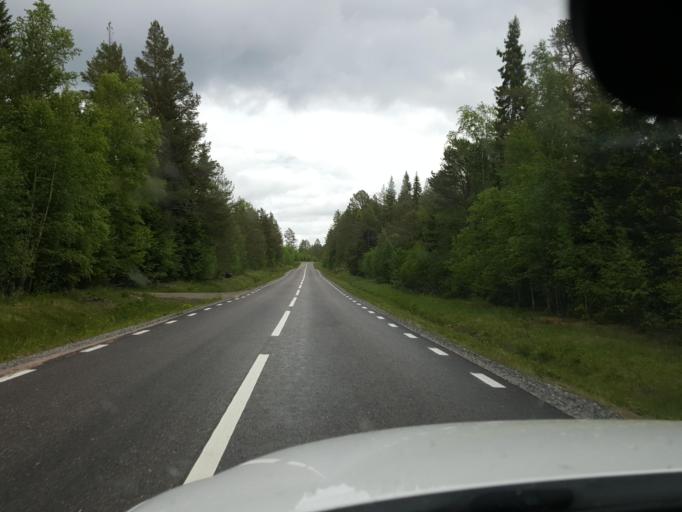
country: SE
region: Gaevleborg
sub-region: Ljusdals Kommun
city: Farila
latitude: 61.7550
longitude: 15.4314
